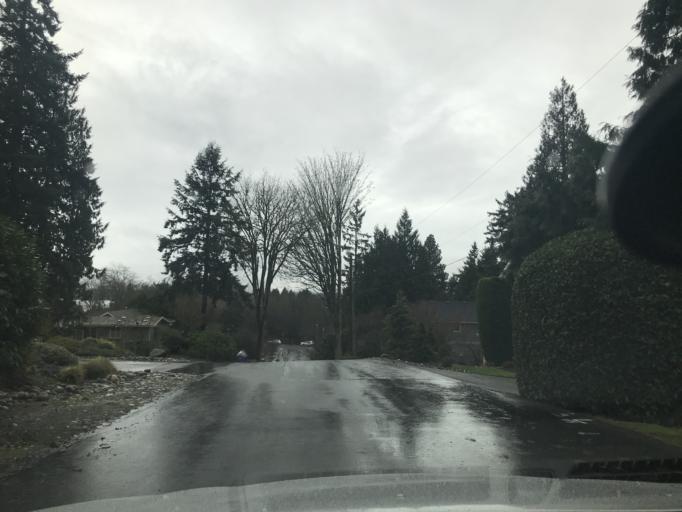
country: US
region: Washington
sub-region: King County
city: Kirkland
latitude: 47.6703
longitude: -122.1828
